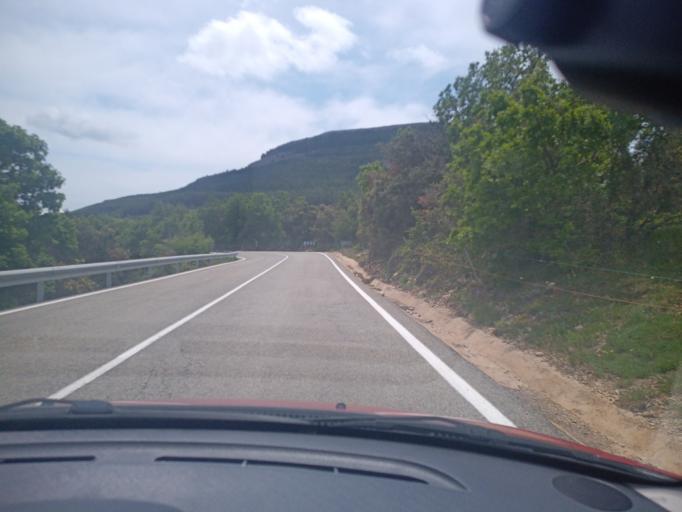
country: ES
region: Valencia
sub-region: Provincia de Castello
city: Ares del Maestre
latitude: 40.4608
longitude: -0.1501
